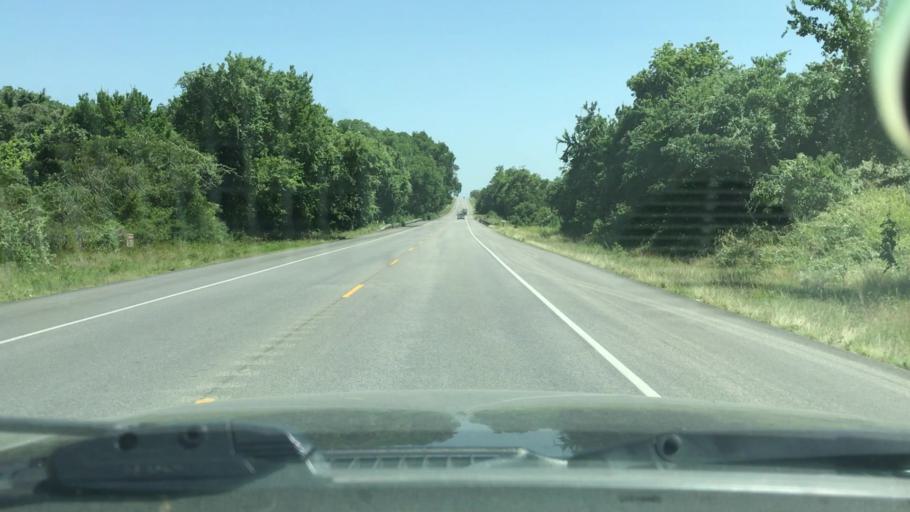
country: US
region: Texas
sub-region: Bastrop County
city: Camp Swift
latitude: 30.2321
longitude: -97.3181
